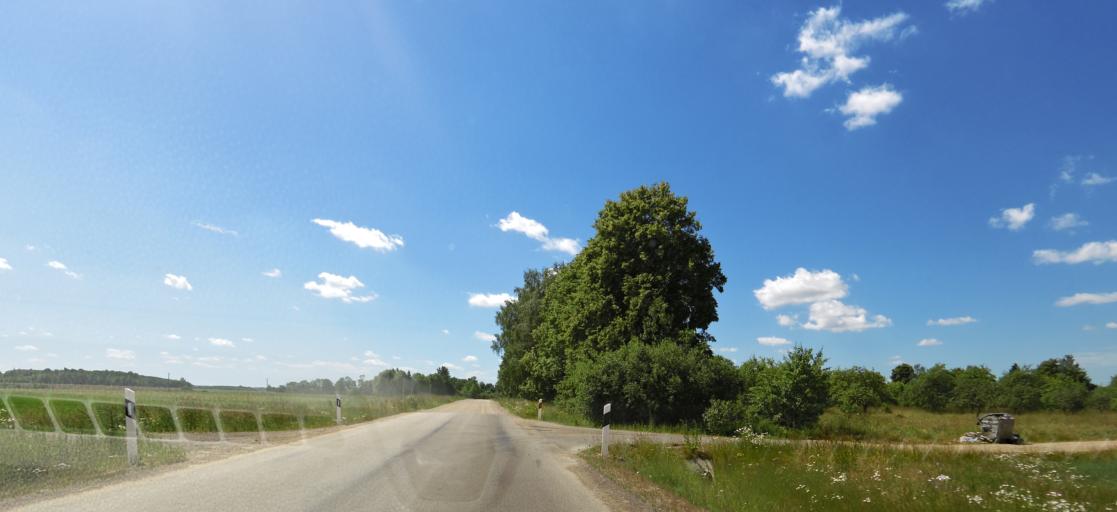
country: LT
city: Kupiskis
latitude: 55.9572
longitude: 24.9877
